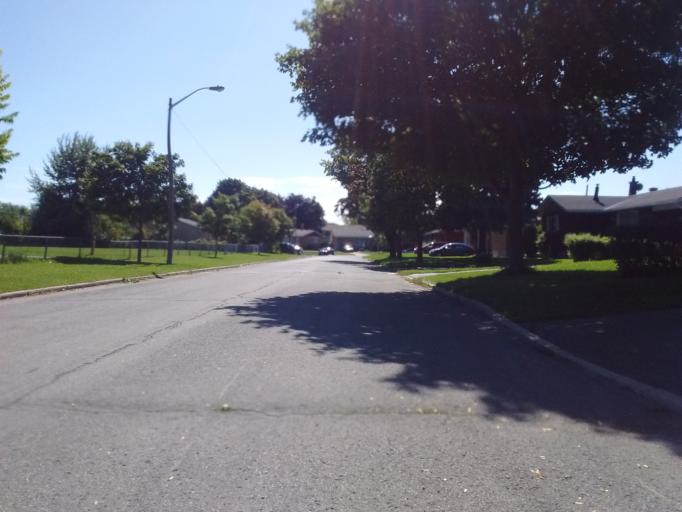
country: CA
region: Ontario
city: Ottawa
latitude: 45.4332
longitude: -75.6377
